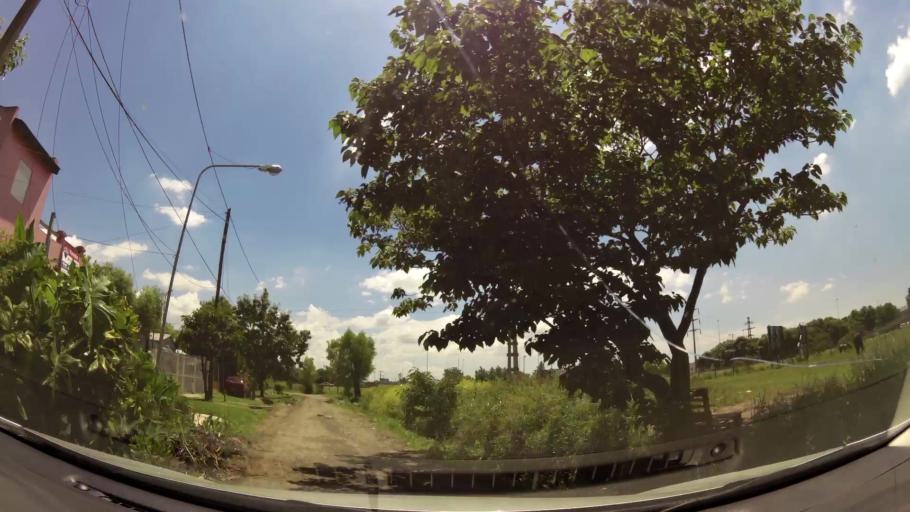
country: AR
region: Buenos Aires
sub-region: Partido de Tigre
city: Tigre
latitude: -34.4390
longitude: -58.5864
